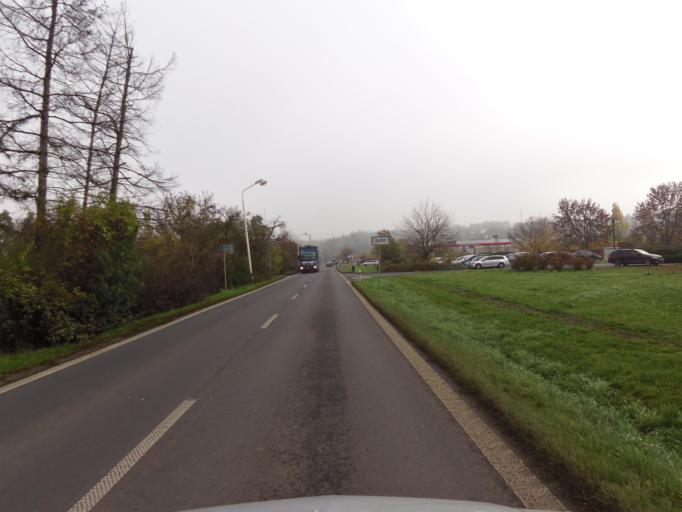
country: CZ
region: Ustecky
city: Zatec
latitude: 50.3241
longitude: 13.5257
